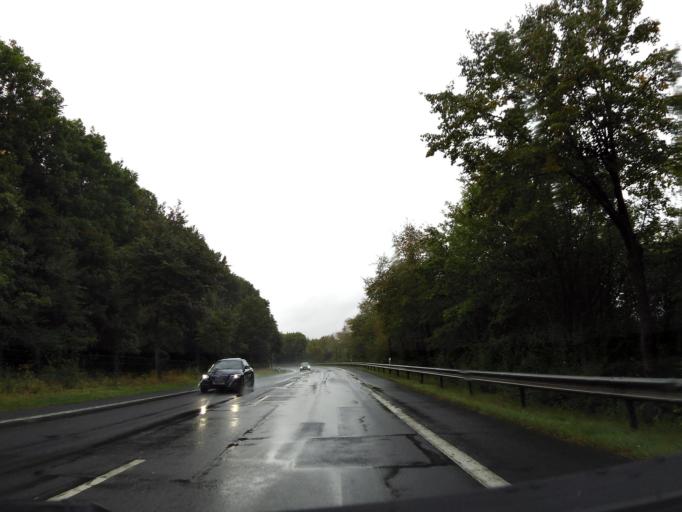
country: DE
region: Lower Saxony
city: Waake
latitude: 51.5614
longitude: 10.0248
